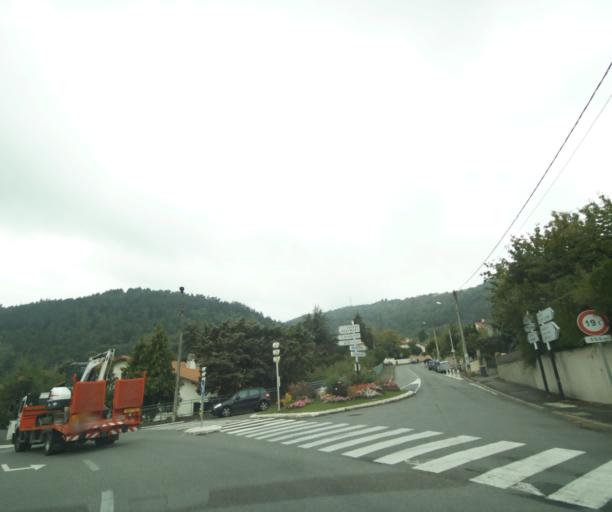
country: FR
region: Auvergne
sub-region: Departement du Puy-de-Dome
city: Ceyrat
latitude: 45.7465
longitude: 3.0594
